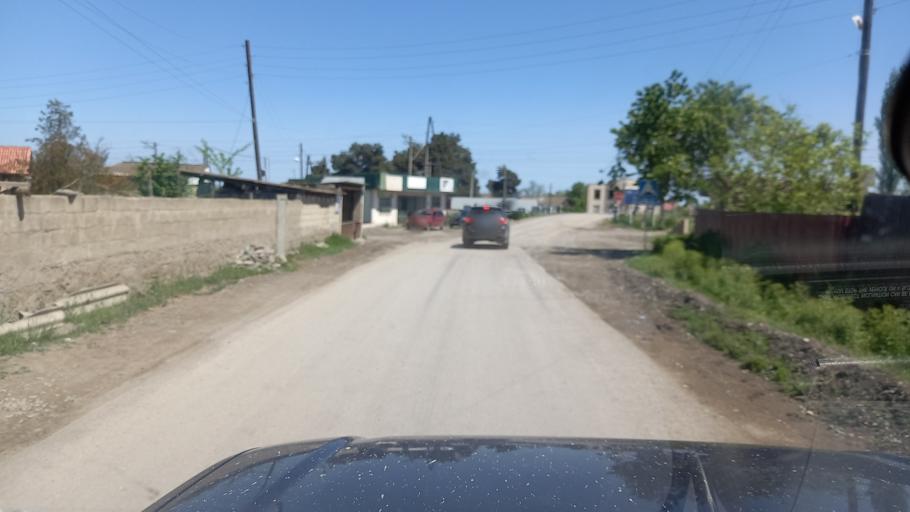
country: RU
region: Dagestan
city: Samur
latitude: 41.8159
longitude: 48.5053
